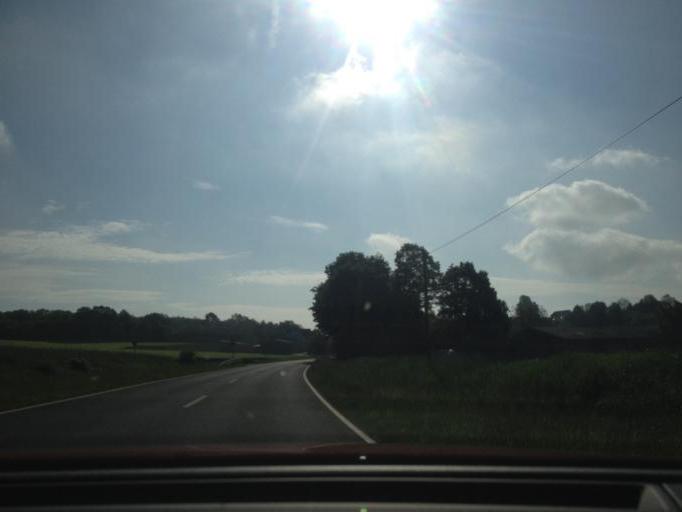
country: DE
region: Bavaria
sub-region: Upper Franconia
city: Prebitz
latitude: 49.7761
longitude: 11.6531
